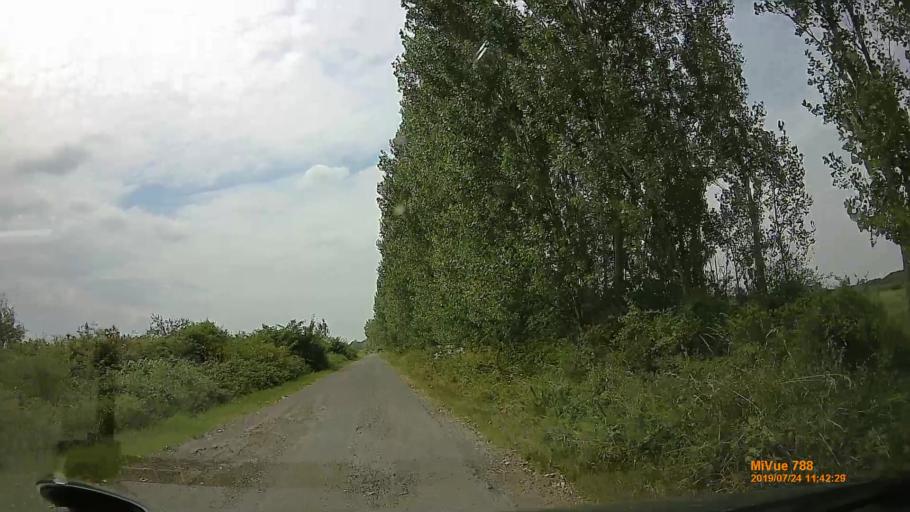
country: UA
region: Zakarpattia
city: Batiovo
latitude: 48.2363
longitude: 22.4587
